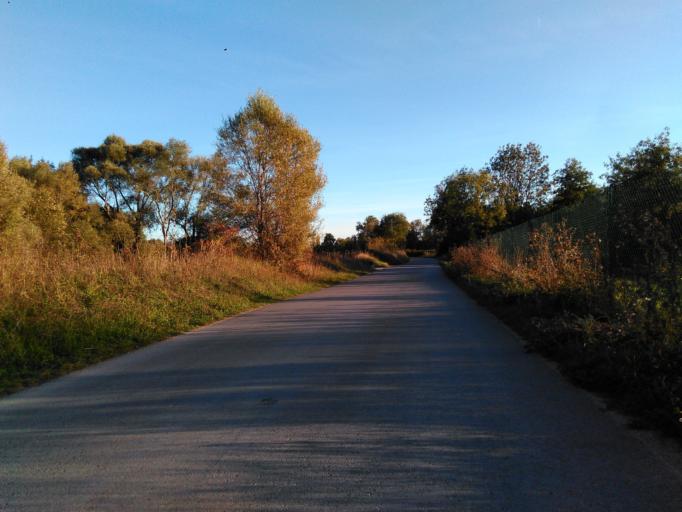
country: FR
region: Lorraine
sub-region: Departement de la Moselle
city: Argancy
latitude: 49.1975
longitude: 6.1854
